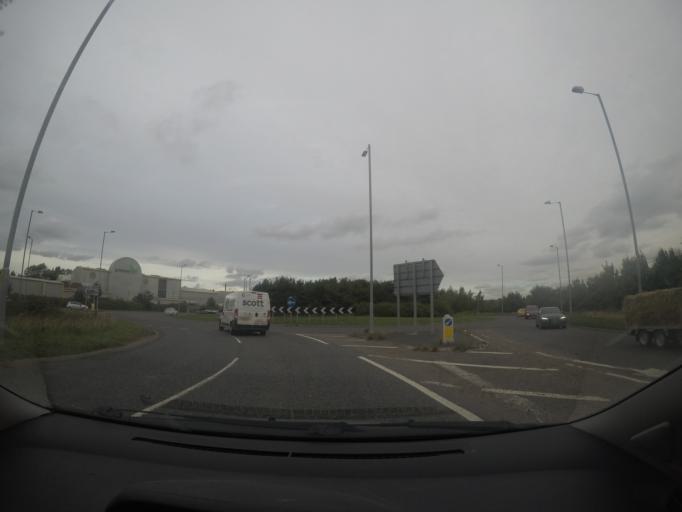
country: GB
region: England
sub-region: North Yorkshire
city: Barlby
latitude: 53.7901
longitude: -1.0398
